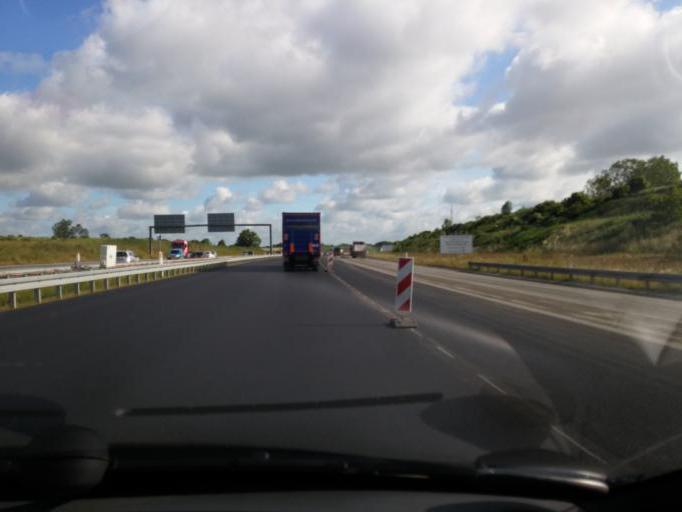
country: DK
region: Zealand
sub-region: Solrod Kommune
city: Solrod
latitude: 55.5292
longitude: 12.1966
